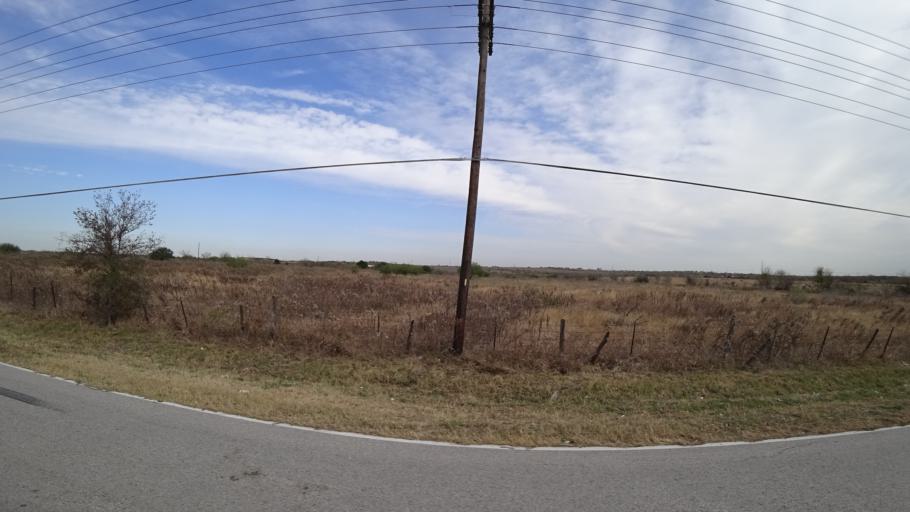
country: US
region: Texas
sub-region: Travis County
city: Onion Creek
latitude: 30.1417
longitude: -97.6859
